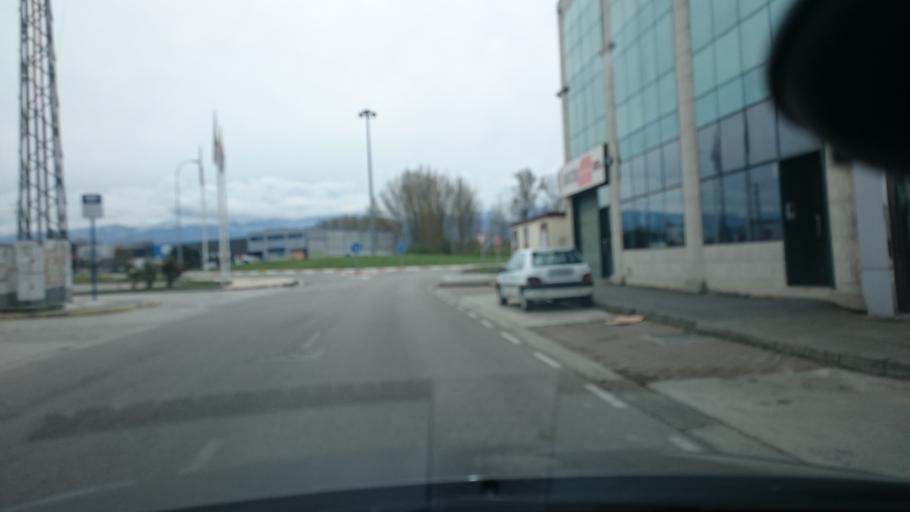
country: ES
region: Castille and Leon
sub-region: Provincia de Leon
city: Camponaraya
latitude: 42.5669
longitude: -6.6586
